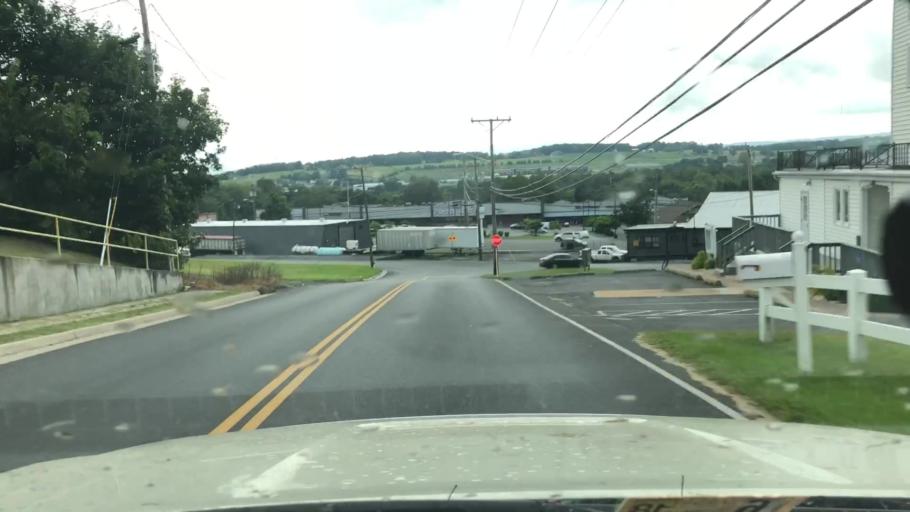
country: US
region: Virginia
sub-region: City of Harrisonburg
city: Harrisonburg
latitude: 38.4319
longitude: -78.8994
